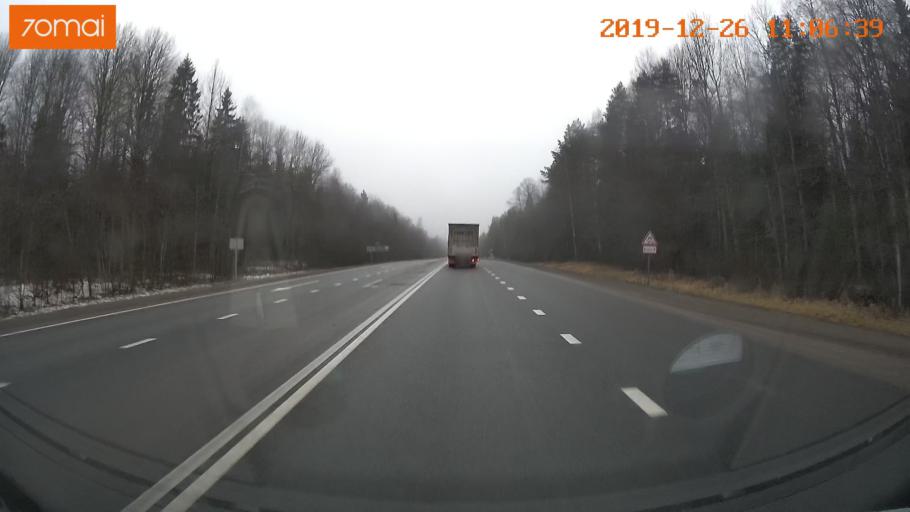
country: RU
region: Vologda
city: Molochnoye
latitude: 59.1417
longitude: 39.3162
